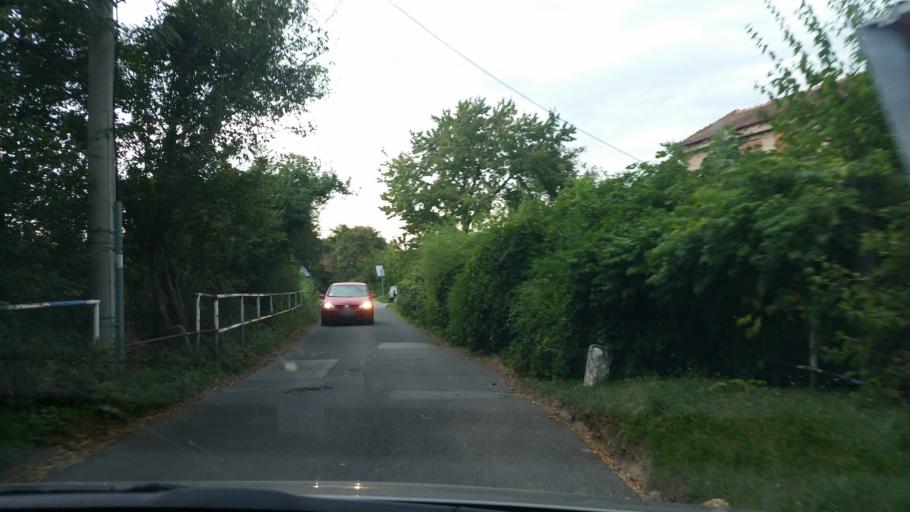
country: RS
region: Central Serbia
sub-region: Belgrade
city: Palilula
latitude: 44.8051
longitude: 20.5020
